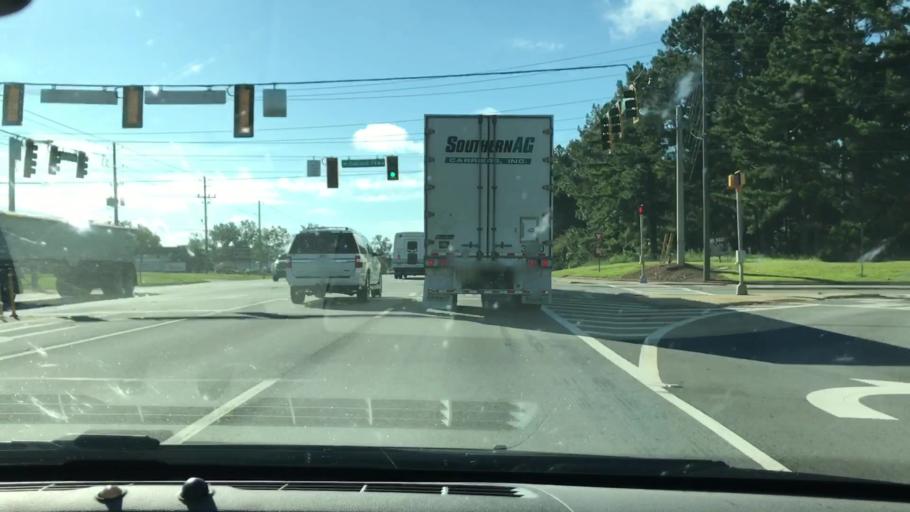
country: US
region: Georgia
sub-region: Dougherty County
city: Albany
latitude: 31.6360
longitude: -84.2468
